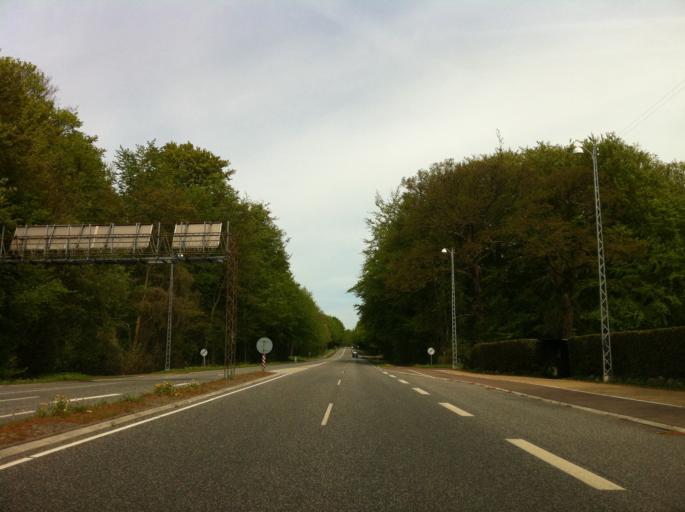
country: DK
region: Capital Region
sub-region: Allerod Kommune
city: Blovstrod
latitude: 55.8756
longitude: 12.3752
